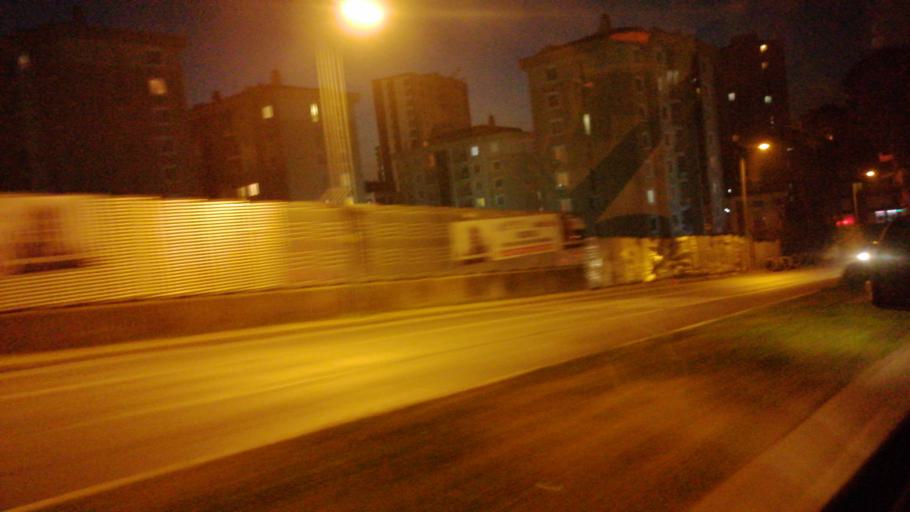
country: TR
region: Istanbul
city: Umraniye
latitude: 41.0068
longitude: 29.1303
